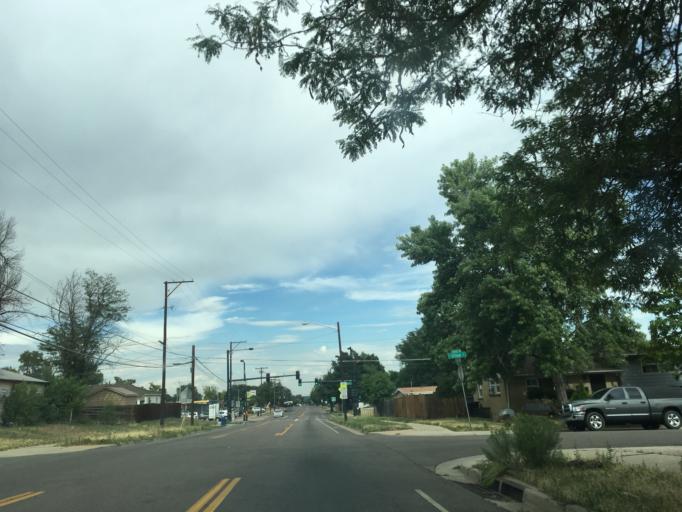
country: US
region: Colorado
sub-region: Jefferson County
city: Lakewood
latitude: 39.6895
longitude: -105.0455
